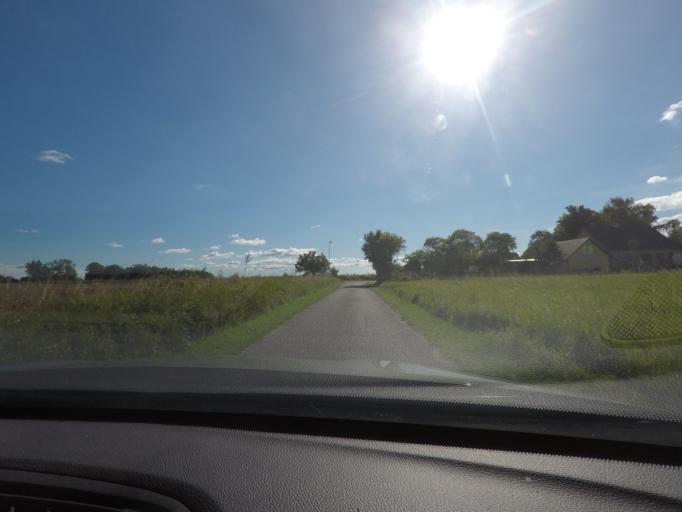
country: DK
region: Zealand
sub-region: Guldborgsund Kommune
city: Sakskobing
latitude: 54.9668
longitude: 11.5362
